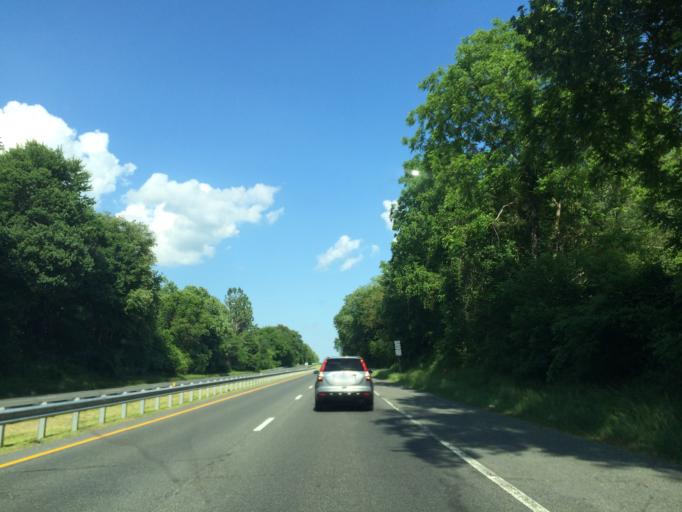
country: US
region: Maryland
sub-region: Howard County
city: Columbia
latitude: 39.2786
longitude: -76.8498
